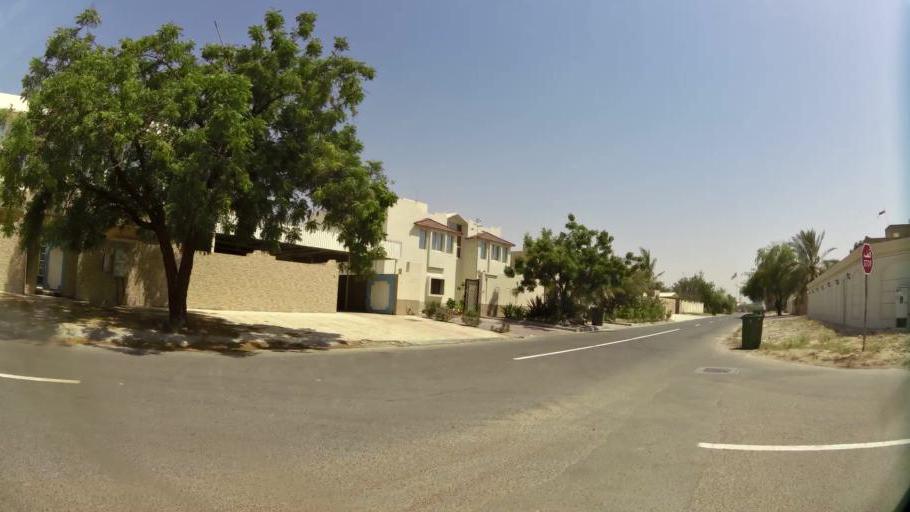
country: AE
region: Ajman
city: Ajman
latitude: 25.4249
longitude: 55.5039
